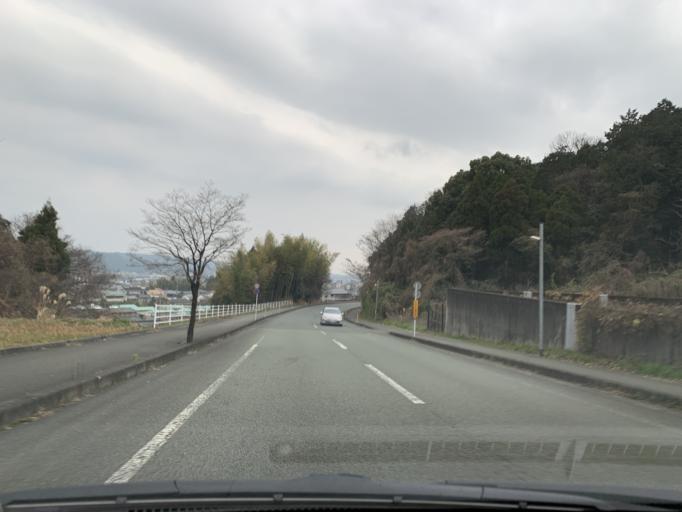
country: JP
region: Kumamoto
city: Ozu
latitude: 32.8835
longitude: 130.8824
